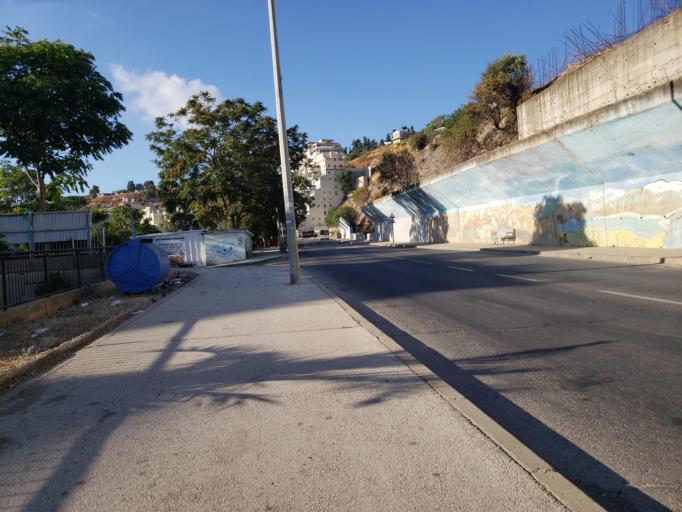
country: IL
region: Northern District
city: Safed
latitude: 32.9622
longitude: 35.4916
